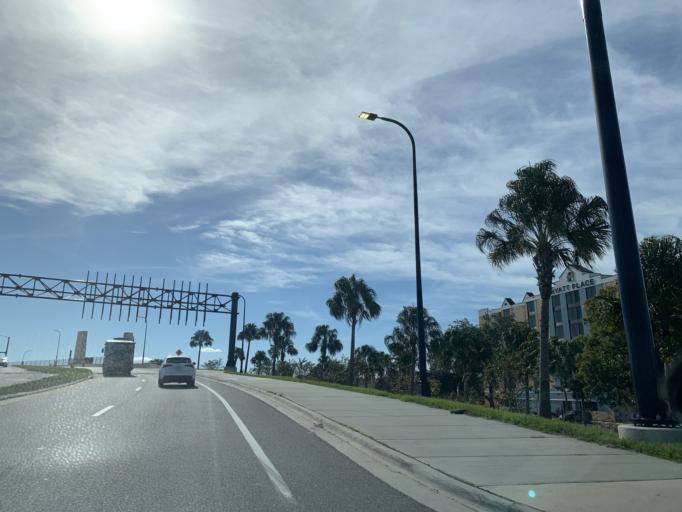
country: US
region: Florida
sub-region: Orange County
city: Tangelo Park
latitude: 28.4754
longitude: -81.4558
